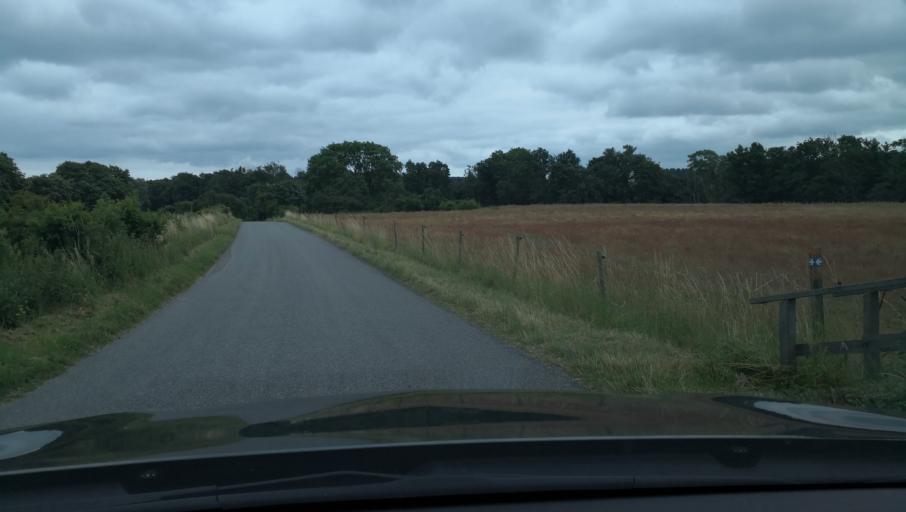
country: SE
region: Skane
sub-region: Simrishamns Kommun
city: Kivik
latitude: 55.7226
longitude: 14.1737
